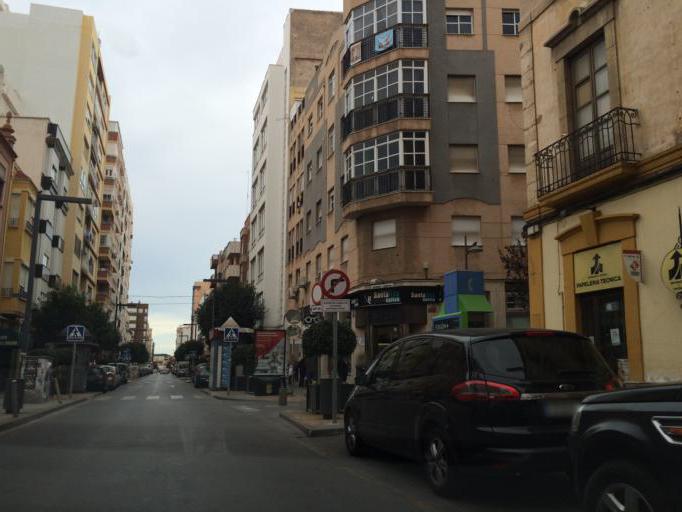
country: ES
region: Andalusia
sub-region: Provincia de Almeria
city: Almeria
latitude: 36.8423
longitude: -2.4606
